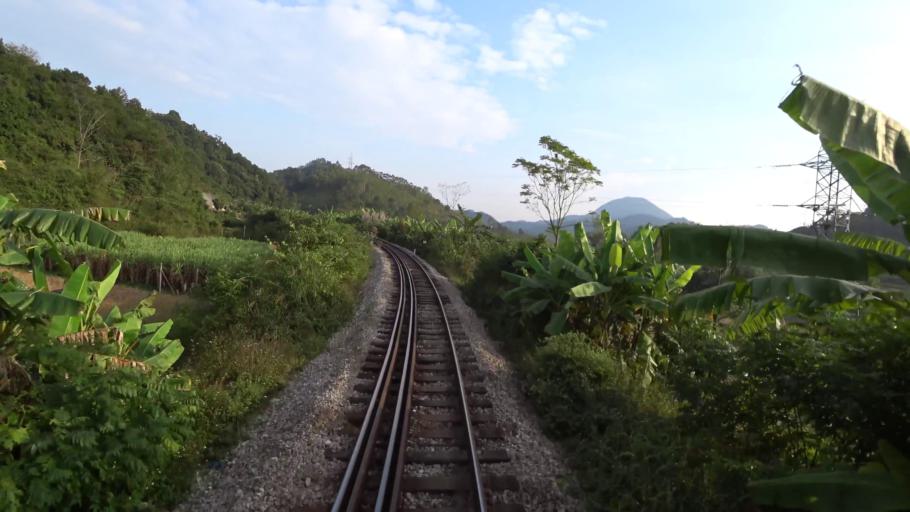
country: VN
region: Lang Son
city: Thi Tran Cao Loc
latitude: 21.9233
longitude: 106.7093
